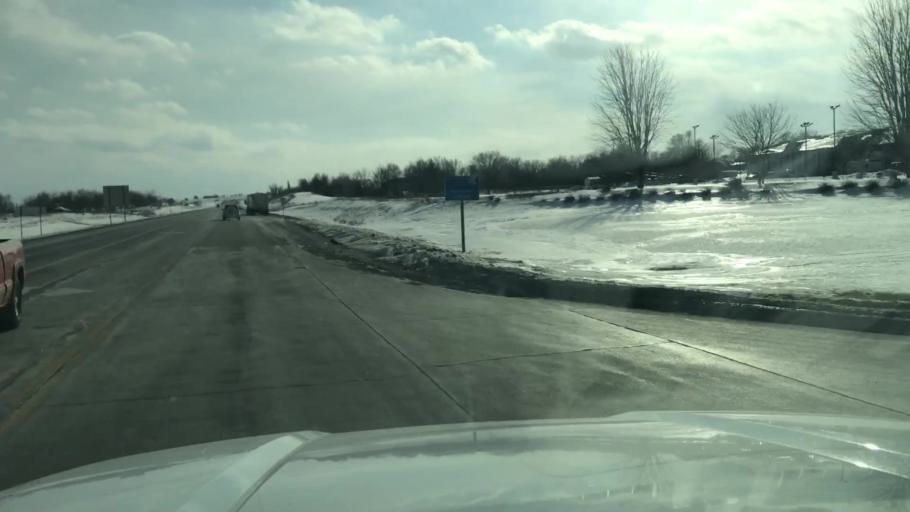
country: US
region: Missouri
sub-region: Nodaway County
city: Maryville
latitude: 40.3451
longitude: -94.8522
